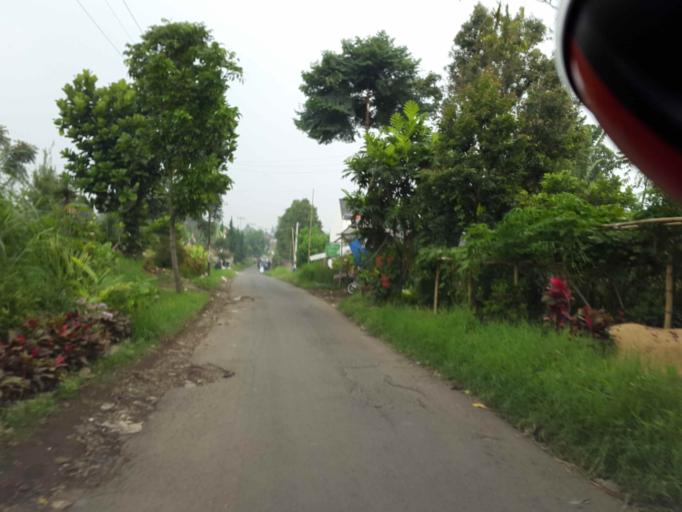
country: ID
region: West Java
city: Lembang
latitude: -6.8261
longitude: 107.5850
